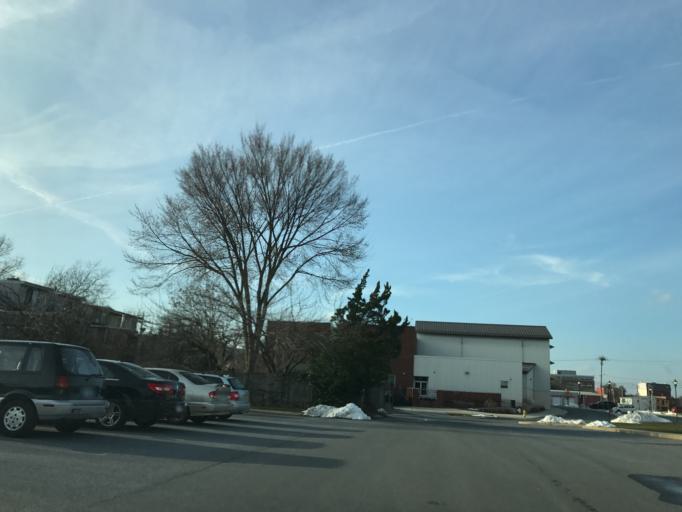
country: US
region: Pennsylvania
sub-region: York County
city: York
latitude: 39.9580
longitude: -76.7325
